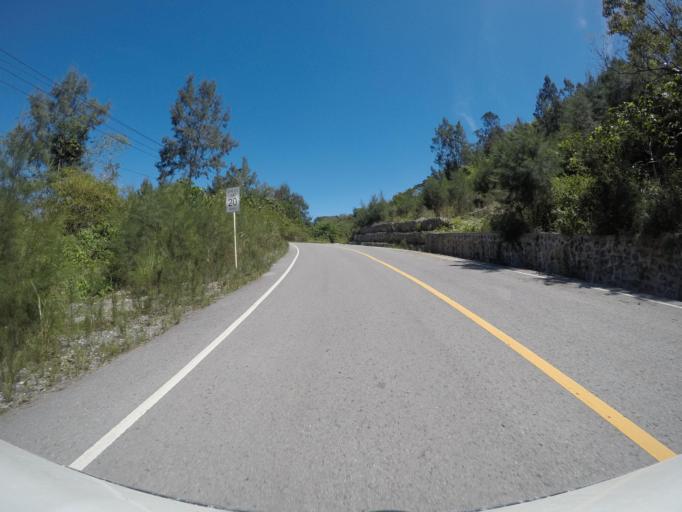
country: TL
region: Manatuto
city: Manatuto
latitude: -8.8087
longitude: 125.9740
